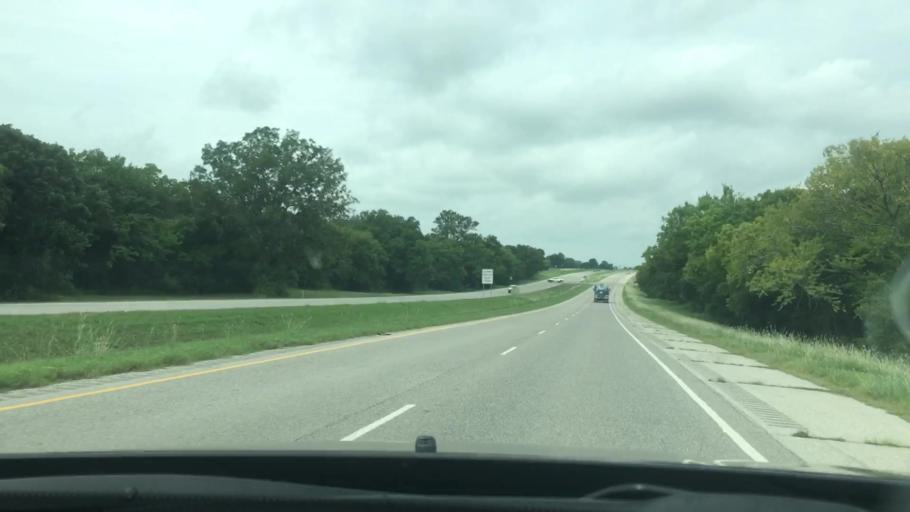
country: US
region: Oklahoma
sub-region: Carter County
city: Wilson
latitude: 34.1730
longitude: -97.4183
